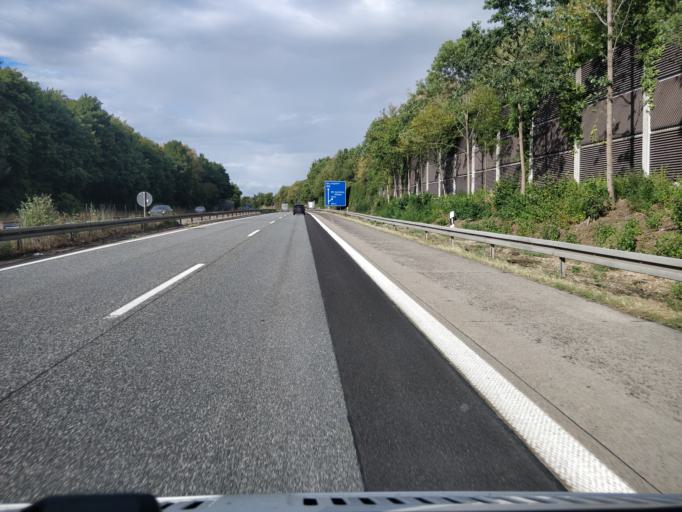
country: DE
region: North Rhine-Westphalia
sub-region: Regierungsbezirk Koln
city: Bonn
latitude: 50.6951
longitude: 7.0616
